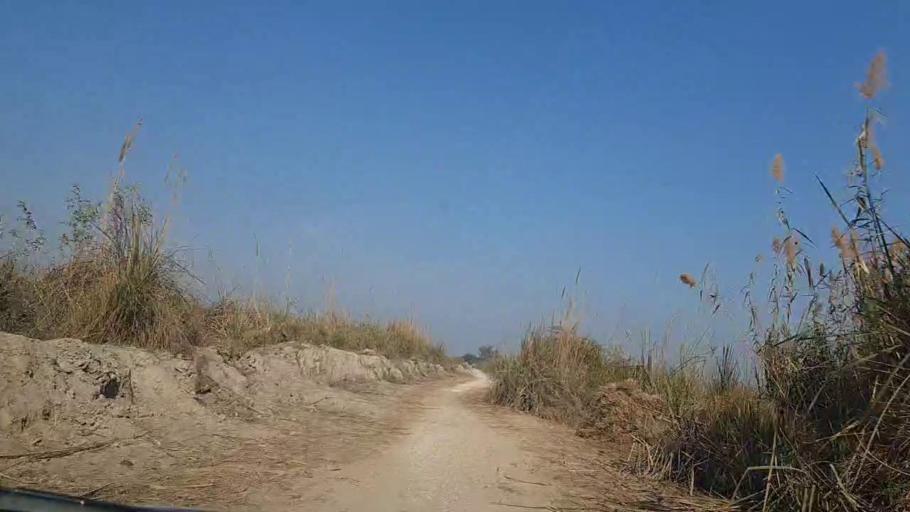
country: PK
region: Sindh
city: Sakrand
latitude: 26.0876
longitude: 68.3664
